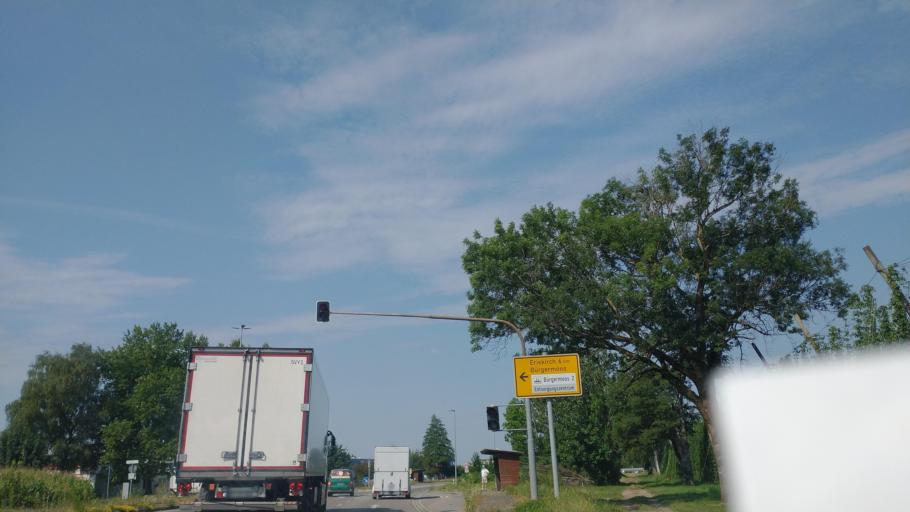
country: DE
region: Baden-Wuerttemberg
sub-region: Tuebingen Region
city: Tettnang
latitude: 47.6649
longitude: 9.5740
